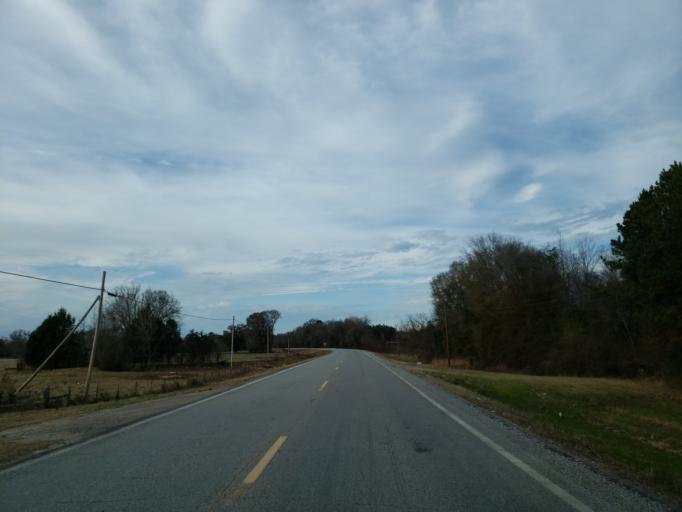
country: US
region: Mississippi
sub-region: Clarke County
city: Quitman
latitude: 31.8679
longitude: -88.7022
